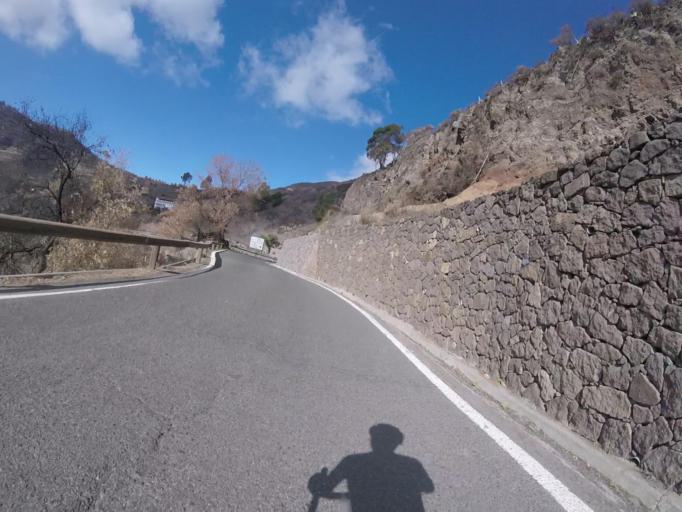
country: ES
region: Canary Islands
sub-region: Provincia de Las Palmas
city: Tejeda
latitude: 28.0094
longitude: -15.5884
